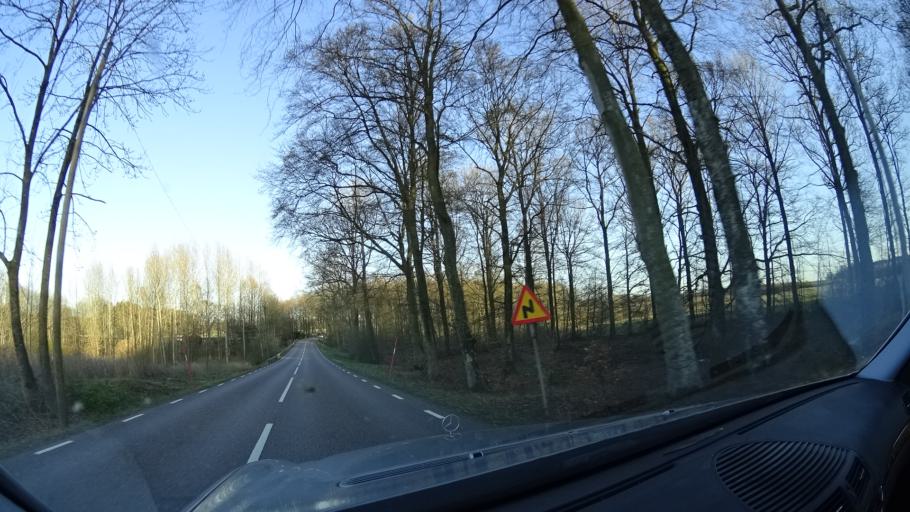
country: SE
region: Skane
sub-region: Svalovs Kommun
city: Kagerod
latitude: 55.9842
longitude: 13.1185
